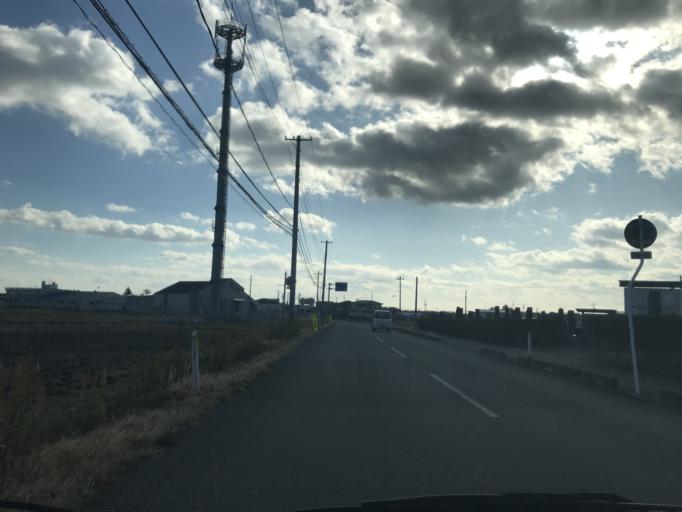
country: JP
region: Iwate
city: Ichinoseki
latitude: 38.7567
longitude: 141.0633
